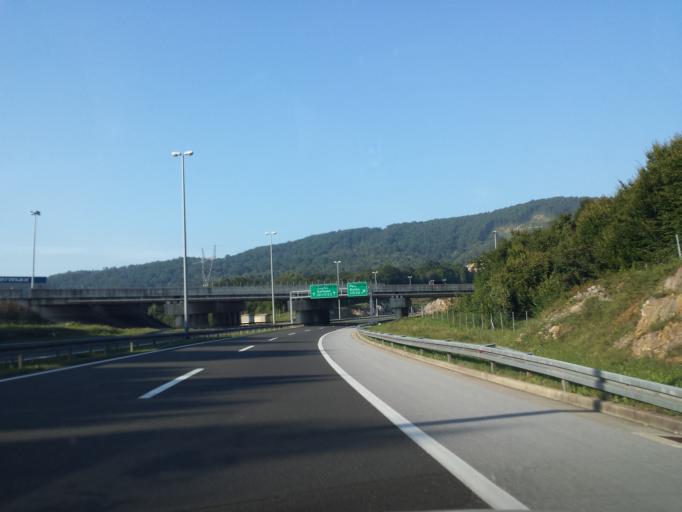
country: HR
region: Karlovacka
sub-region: Grad Ogulin
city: Ogulin
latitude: 45.4047
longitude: 15.2496
